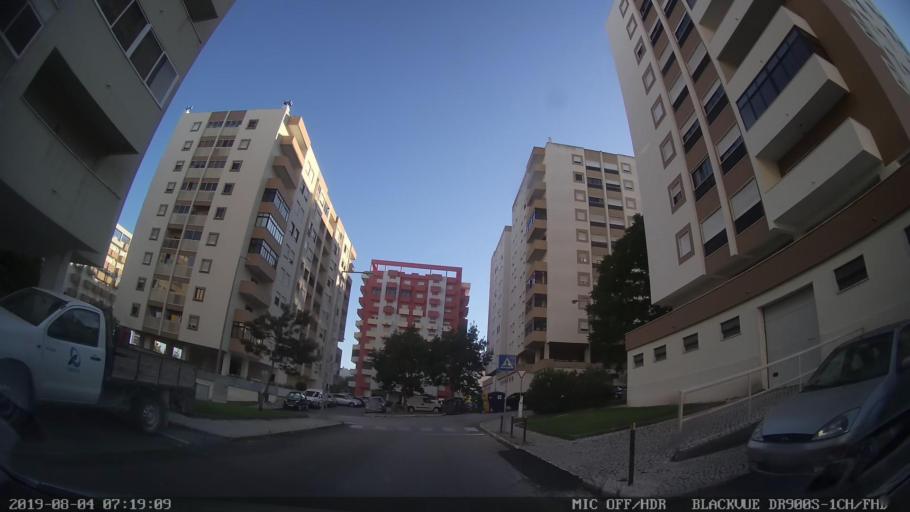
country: PT
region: Lisbon
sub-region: Vila Franca de Xira
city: Vialonga
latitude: 38.8663
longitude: -9.0666
